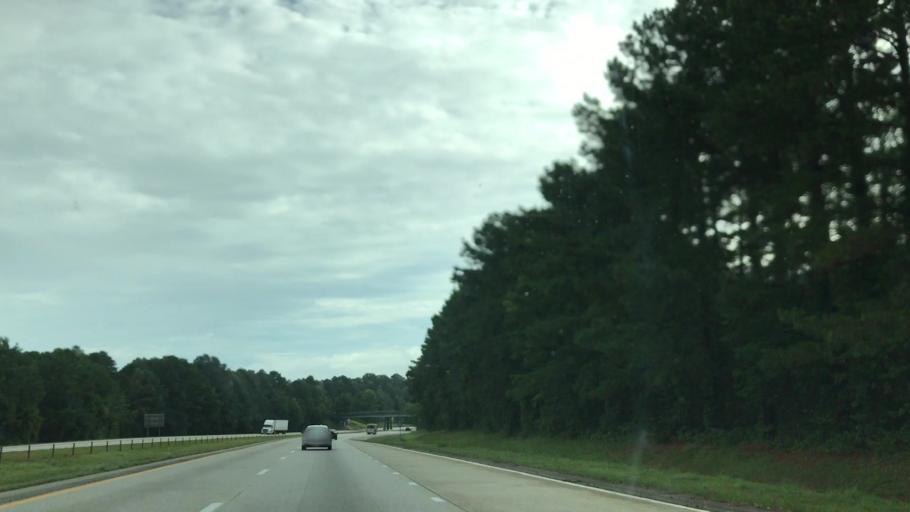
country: US
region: North Carolina
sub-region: Nash County
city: Red Oak
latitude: 36.0190
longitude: -77.8591
